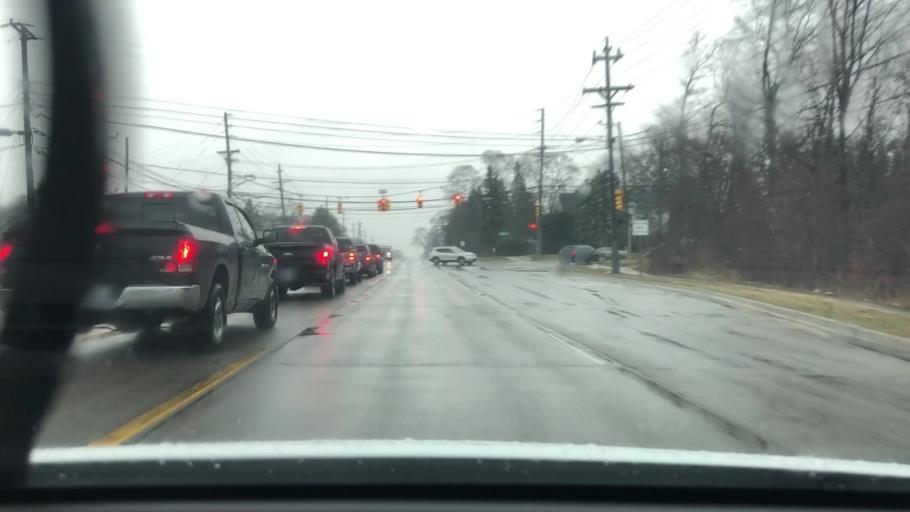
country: US
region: Michigan
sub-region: Oakland County
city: Troy
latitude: 42.5774
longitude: -83.1681
